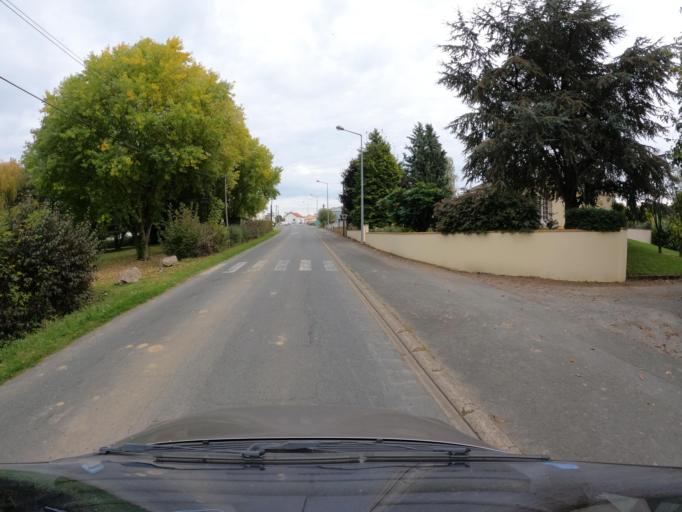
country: FR
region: Pays de la Loire
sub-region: Departement de Maine-et-Loire
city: Saint-Christophe-du-Bois
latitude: 47.0261
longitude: -0.9500
